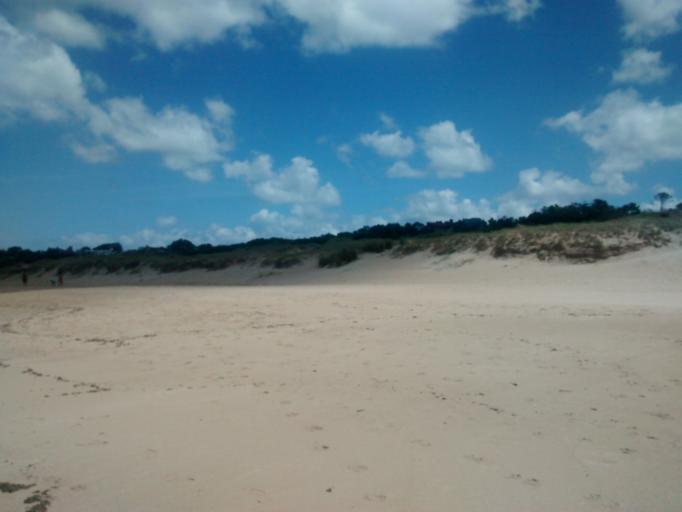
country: UY
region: Maldonado
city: Piriapolis
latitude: -34.9007
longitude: -55.2499
